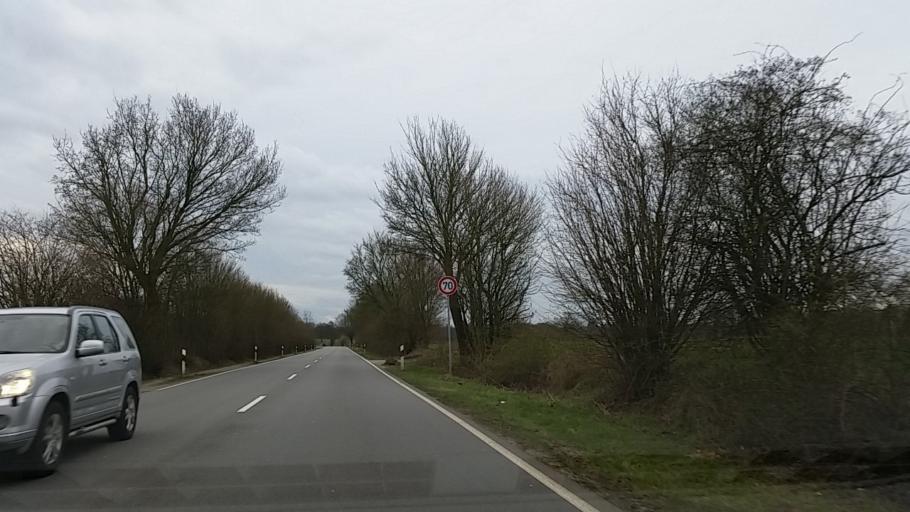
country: DE
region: Schleswig-Holstein
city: Braak
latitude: 53.6068
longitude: 10.2412
